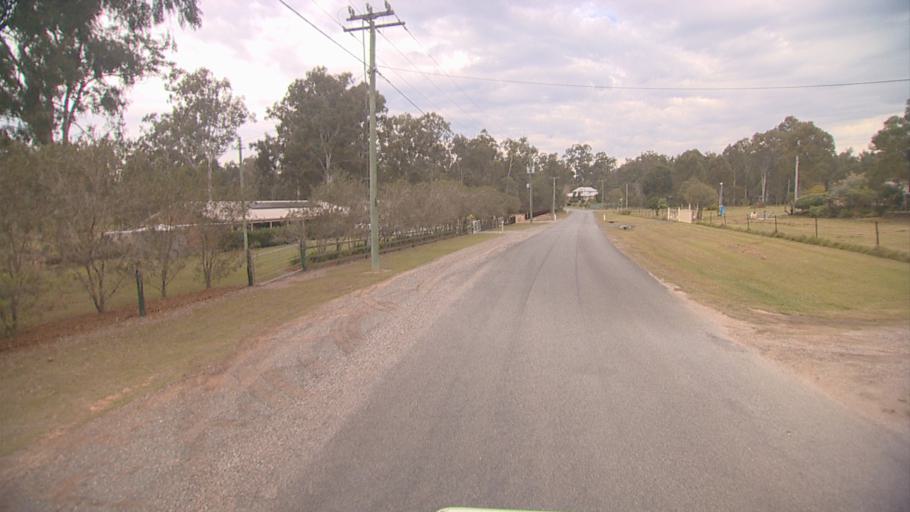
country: AU
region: Queensland
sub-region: Logan
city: Chambers Flat
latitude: -27.7893
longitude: 153.1155
